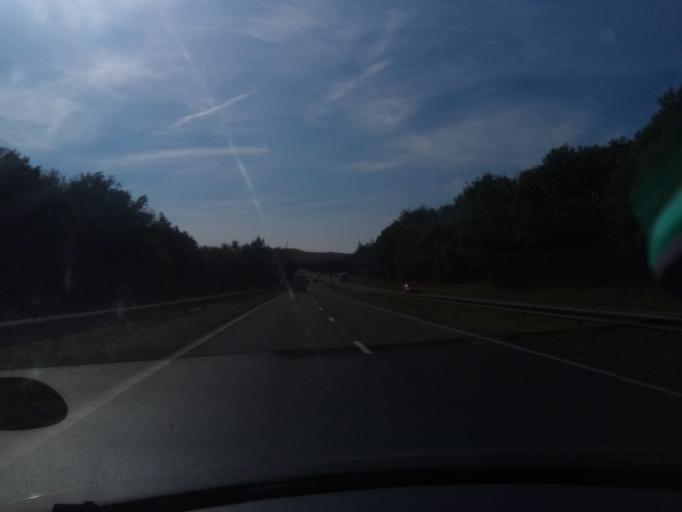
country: GB
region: England
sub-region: County Durham
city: Hawthorn
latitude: 54.8108
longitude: -1.3610
